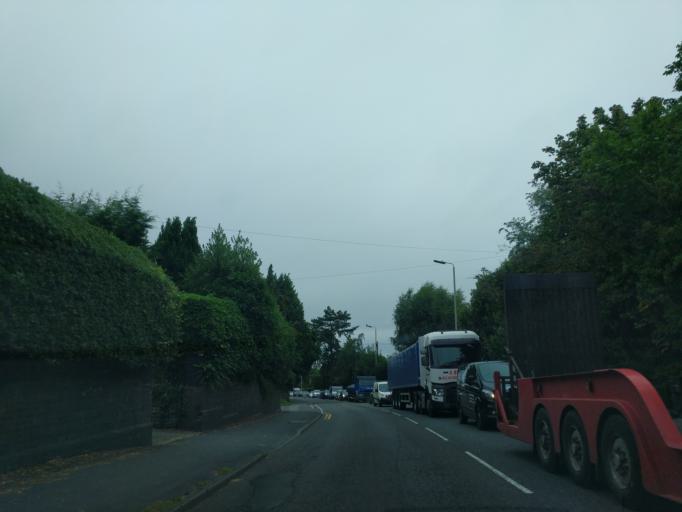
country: GB
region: England
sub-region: Worcestershire
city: Hagley
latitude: 52.4398
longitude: -2.1337
